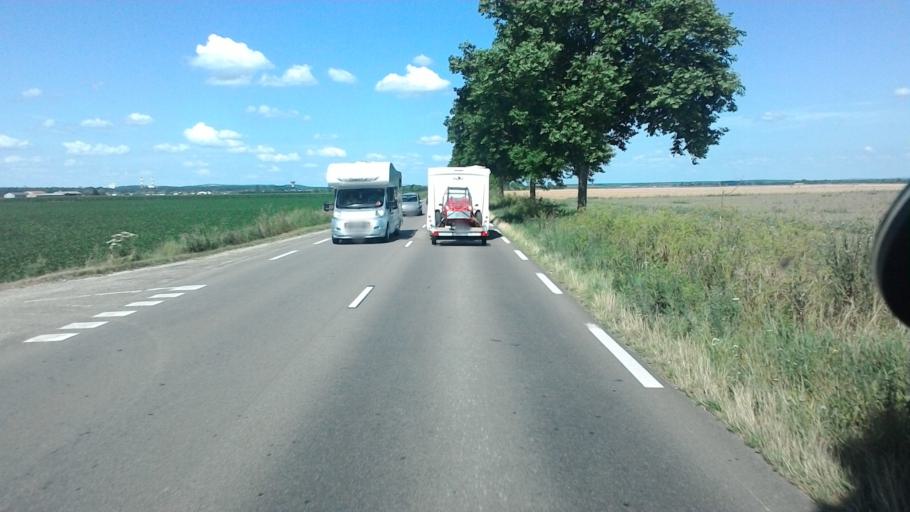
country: FR
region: Franche-Comte
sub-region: Departement du Jura
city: Tavaux
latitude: 47.0218
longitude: 5.3854
